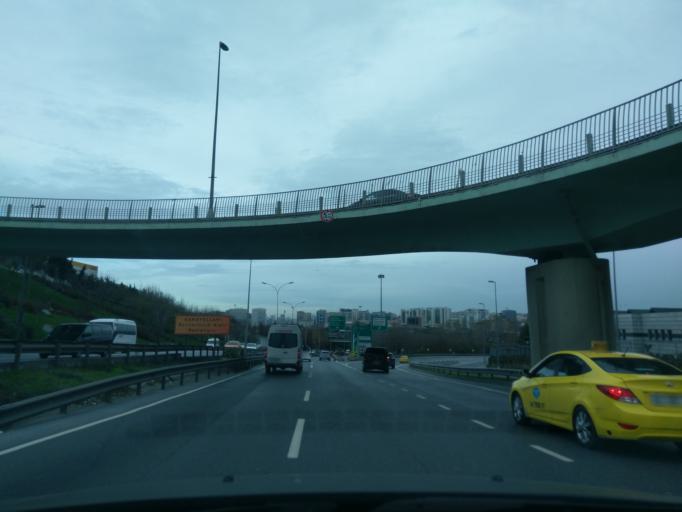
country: TR
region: Istanbul
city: Bahcelievler
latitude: 40.9886
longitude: 28.8187
